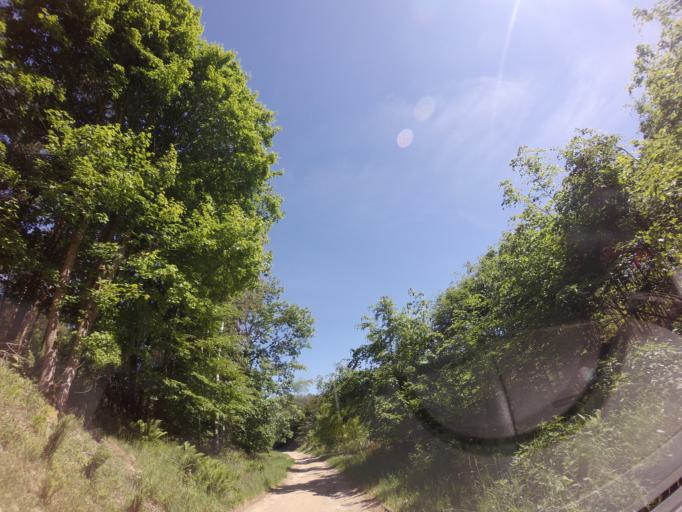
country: PL
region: West Pomeranian Voivodeship
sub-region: Powiat choszczenski
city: Recz
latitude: 53.3021
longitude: 15.5979
